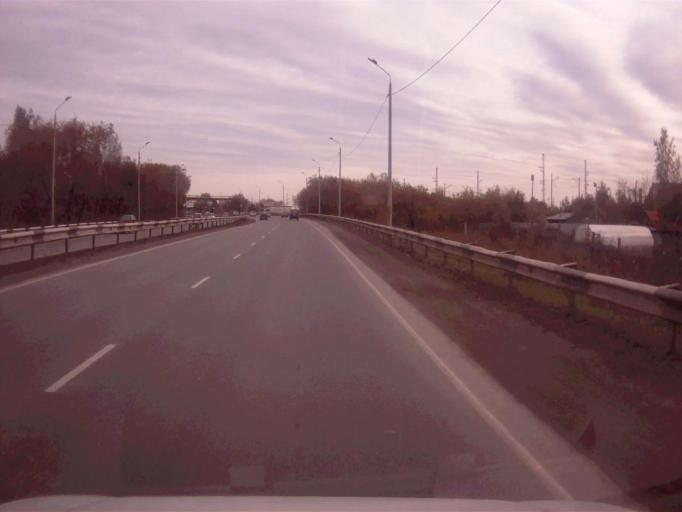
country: RU
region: Chelyabinsk
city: Novosineglazovskiy
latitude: 55.0439
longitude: 61.4234
